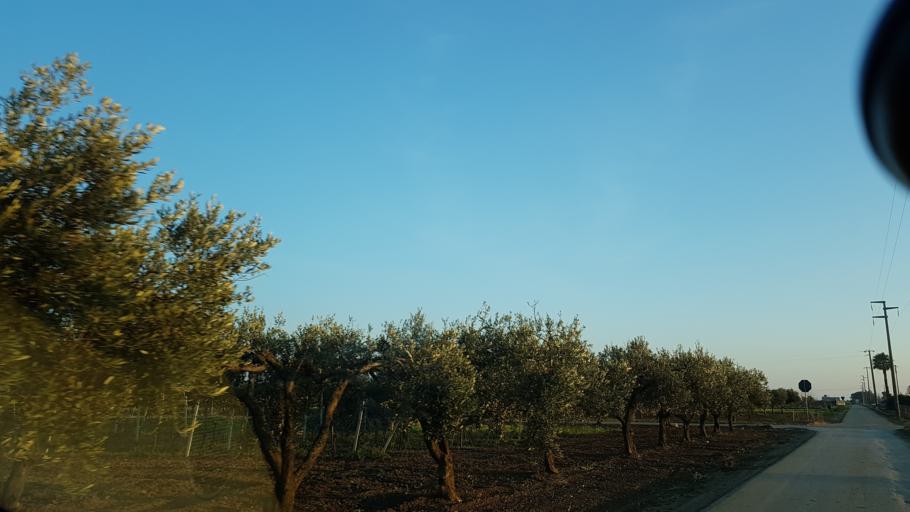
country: IT
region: Apulia
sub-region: Provincia di Brindisi
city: La Rosa
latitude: 40.5913
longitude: 17.9350
